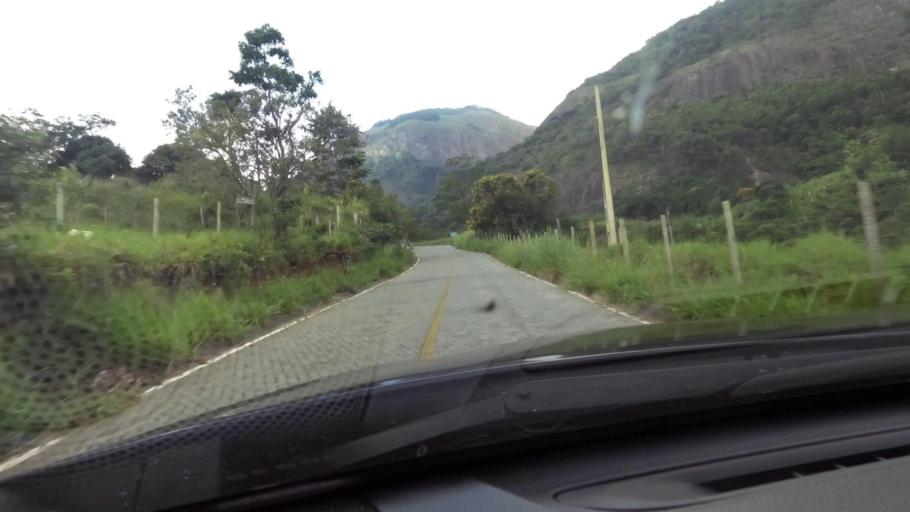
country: BR
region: Espirito Santo
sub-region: Guarapari
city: Guarapari
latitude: -20.6036
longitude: -40.5367
